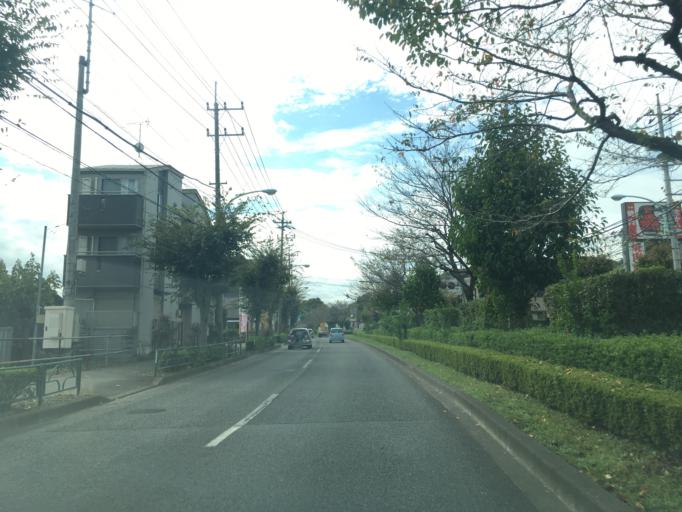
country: JP
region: Tokyo
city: Hino
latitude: 35.6365
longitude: 139.4137
